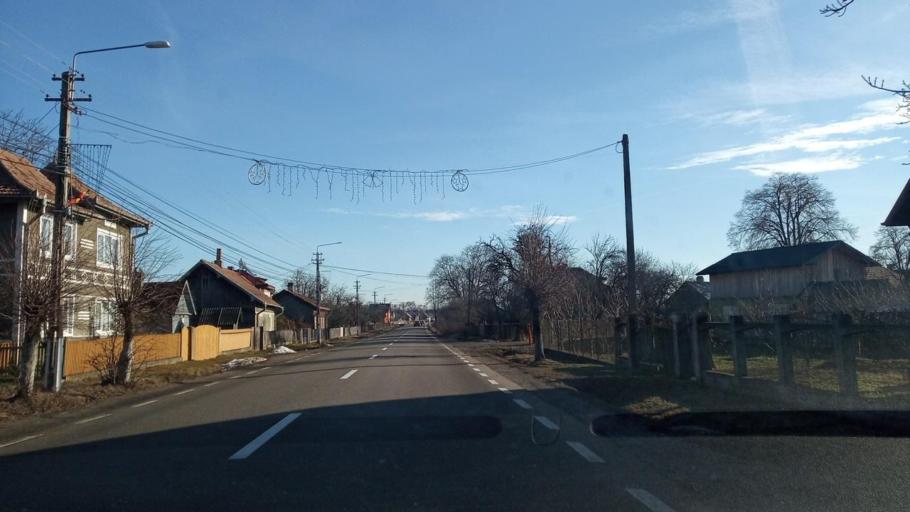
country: RO
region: Suceava
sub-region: Comuna Paltinoasa
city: Capu Codrului
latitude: 47.5344
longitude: 25.9768
